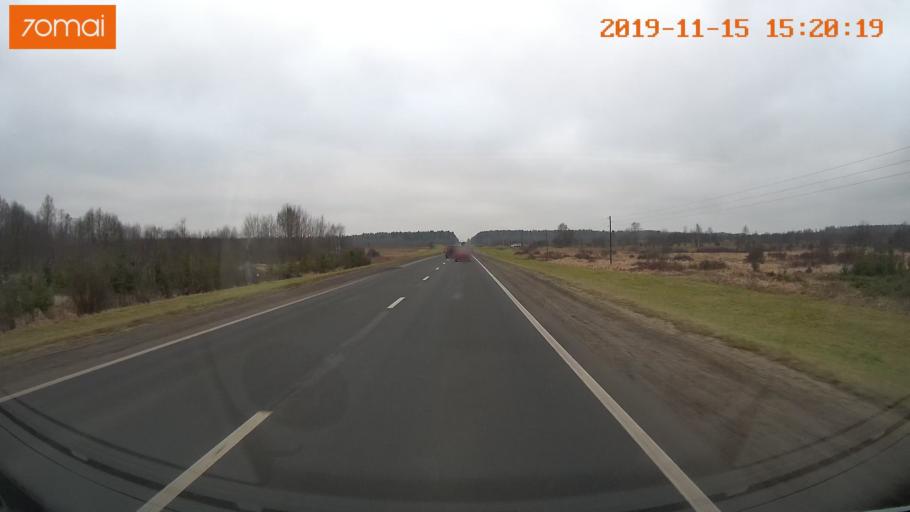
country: RU
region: Jaroslavl
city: Danilov
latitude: 58.2249
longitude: 40.1638
